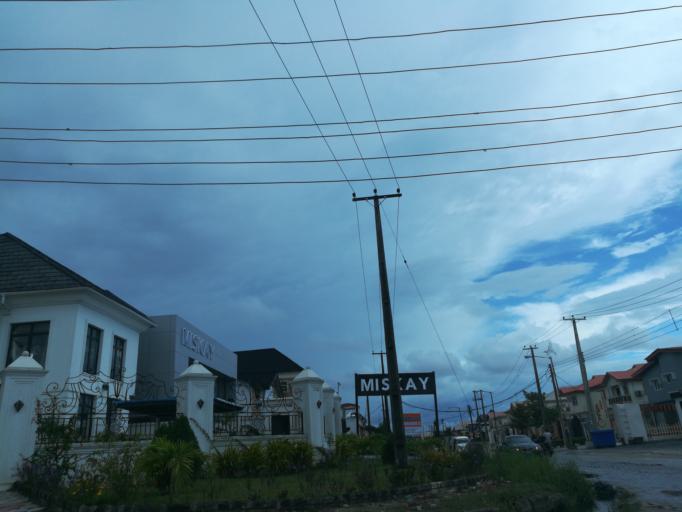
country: NG
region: Lagos
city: Ikoyi
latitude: 6.4428
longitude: 3.4765
